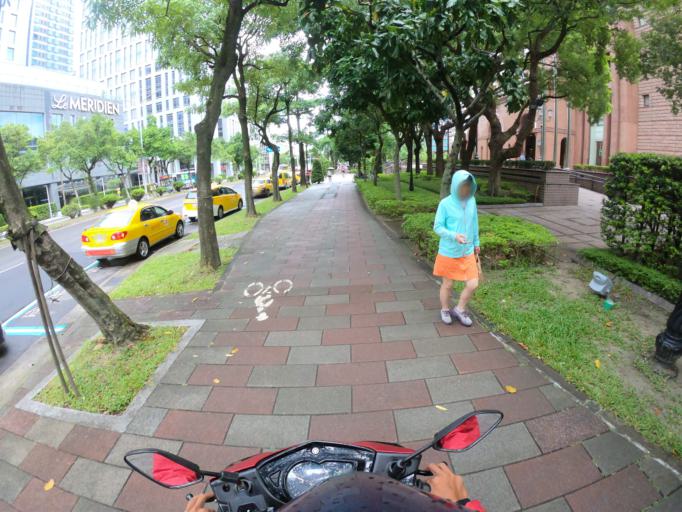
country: TW
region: Taipei
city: Taipei
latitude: 25.0378
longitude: 121.5686
